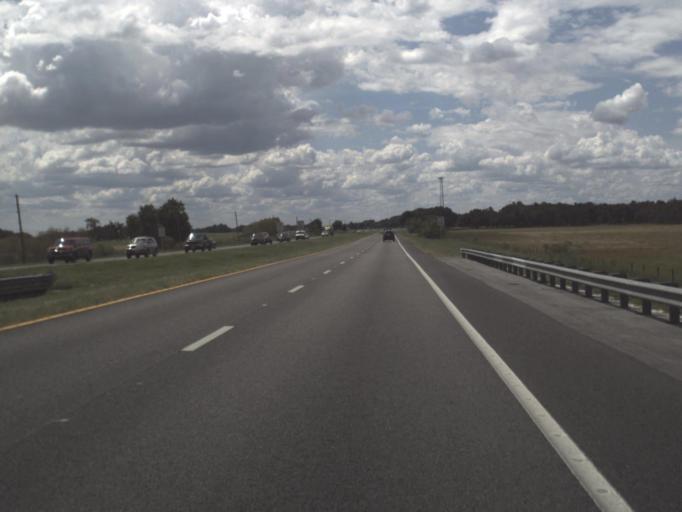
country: US
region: Florida
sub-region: Polk County
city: Alturas
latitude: 27.9134
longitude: -81.6984
